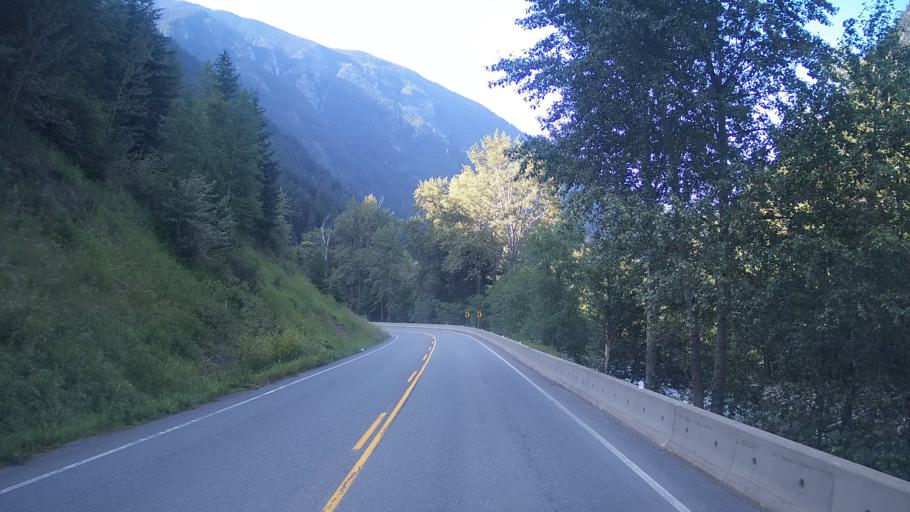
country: CA
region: British Columbia
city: Lillooet
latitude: 50.5741
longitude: -122.0882
